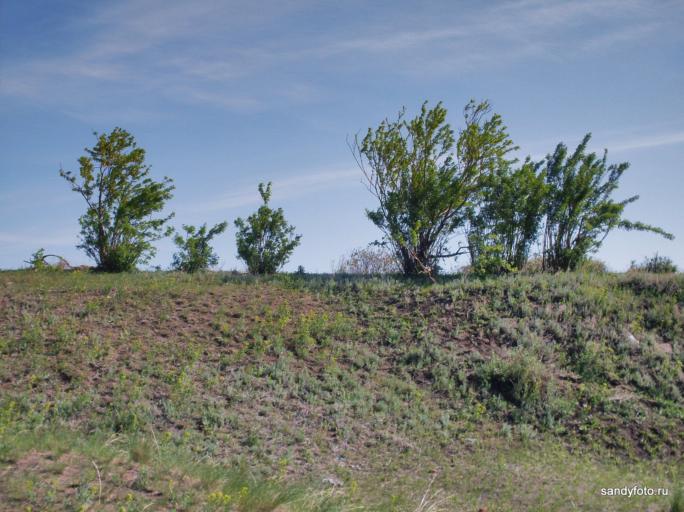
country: RU
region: Chelyabinsk
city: Troitsk
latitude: 54.1345
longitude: 61.4358
